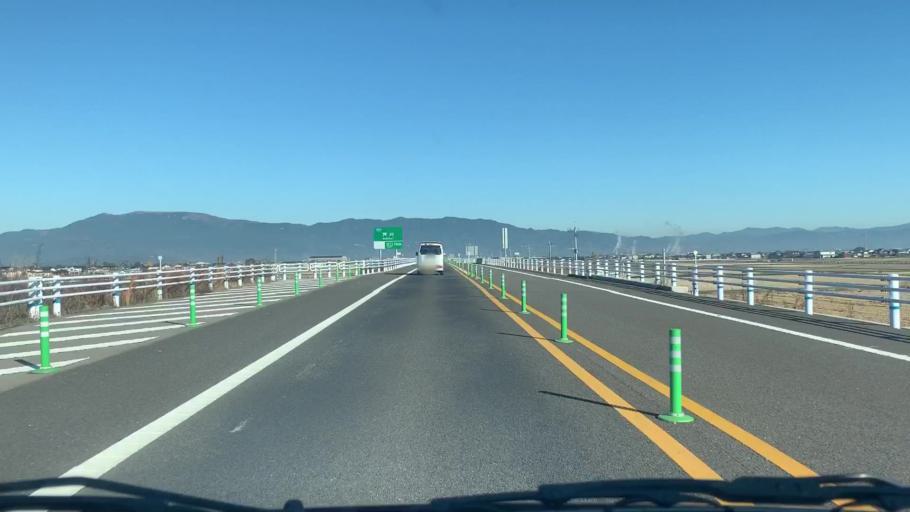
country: JP
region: Saga Prefecture
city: Saga-shi
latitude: 33.2087
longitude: 130.2150
